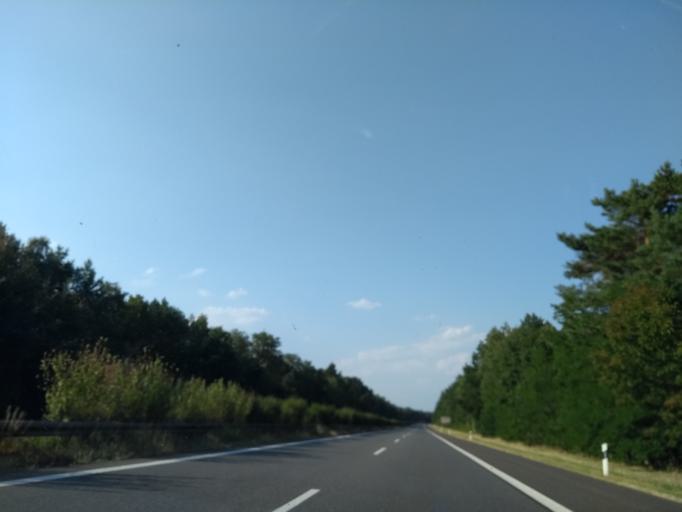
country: DE
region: Brandenburg
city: Calau
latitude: 51.8005
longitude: 13.8840
